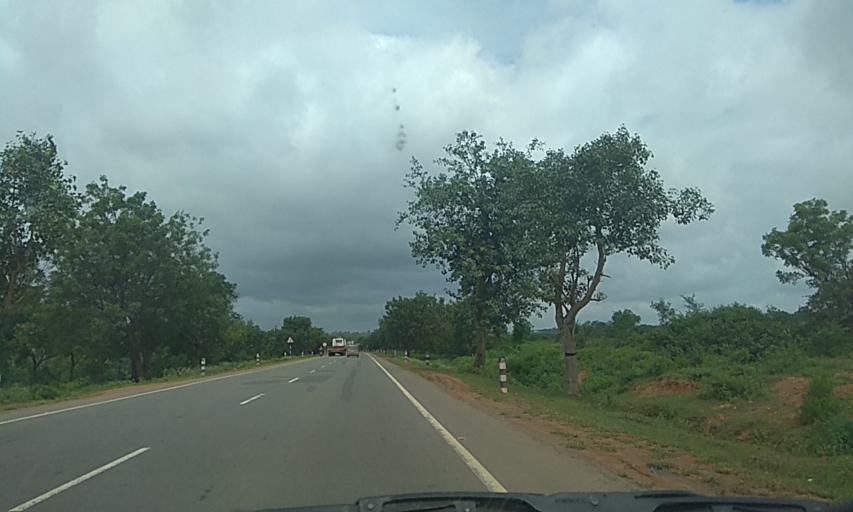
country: IN
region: Karnataka
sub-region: Dharwad
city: Hubli
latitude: 15.3327
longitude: 75.0996
